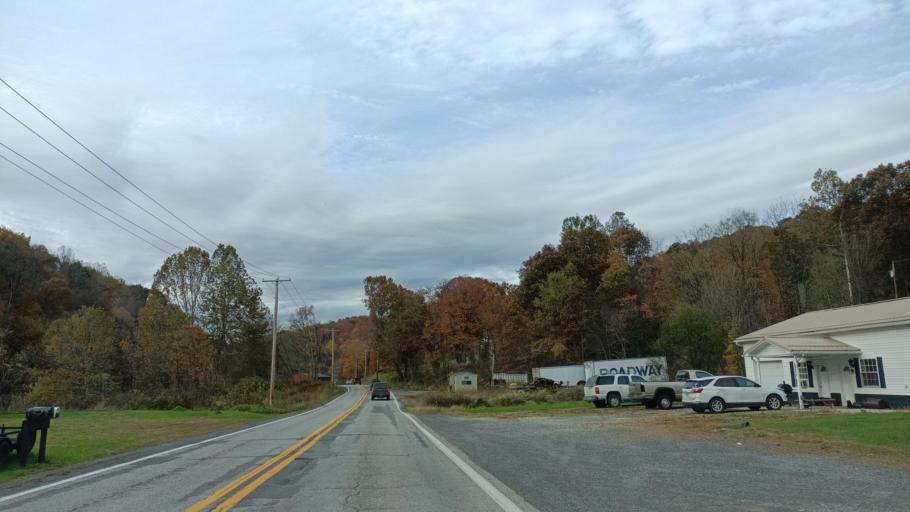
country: US
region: West Virginia
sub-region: Taylor County
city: Grafton
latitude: 39.3331
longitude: -79.8489
